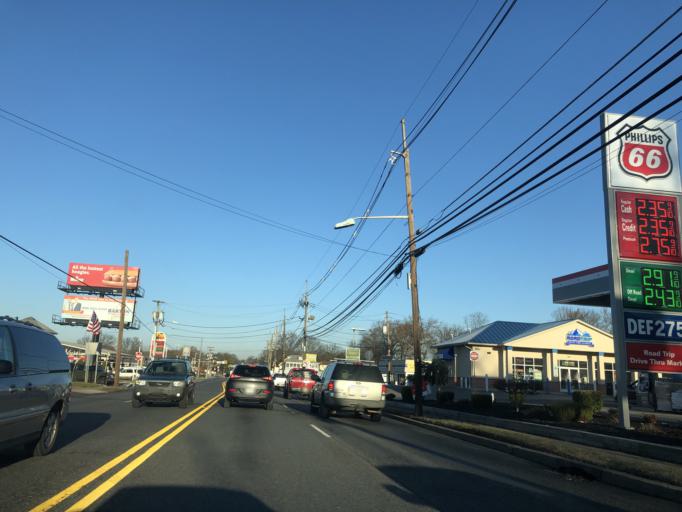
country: US
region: New Jersey
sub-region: Camden County
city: Barrington
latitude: 39.8712
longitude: -75.0440
